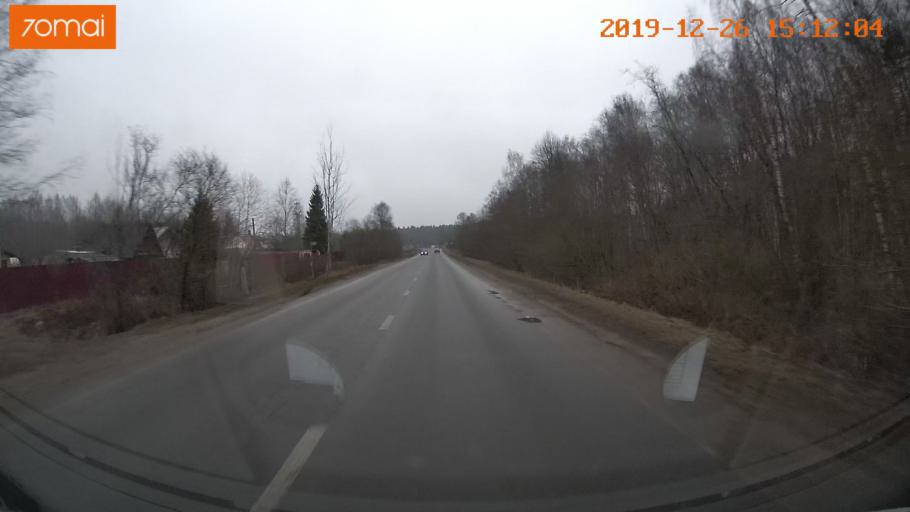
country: RU
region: Jaroslavl
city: Rybinsk
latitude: 58.1306
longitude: 38.8701
